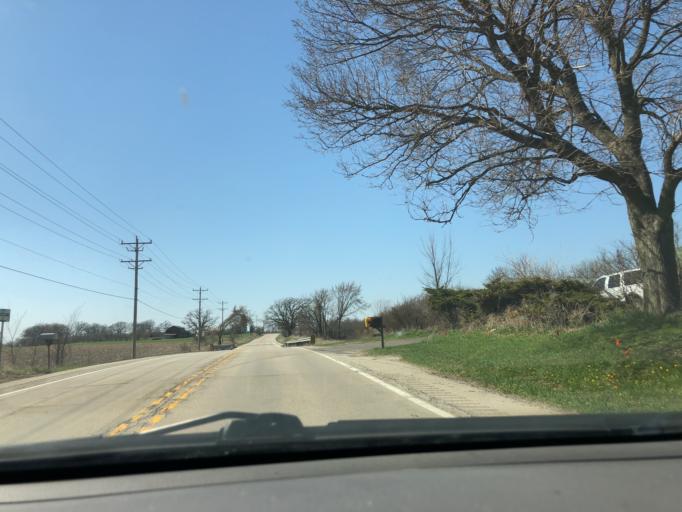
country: US
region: Illinois
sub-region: Kane County
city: Hampshire
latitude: 42.1308
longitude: -88.4920
